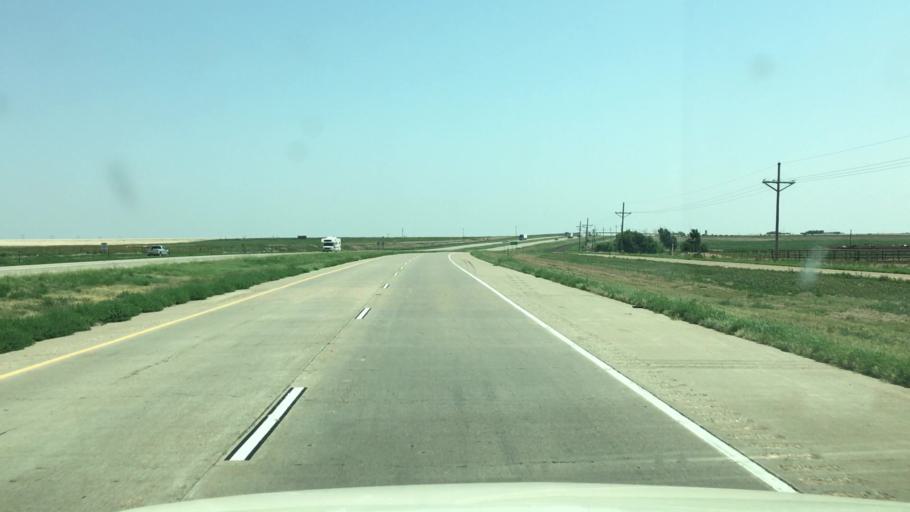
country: US
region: Texas
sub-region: Potter County
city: Bushland
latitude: 35.2087
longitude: -102.1707
